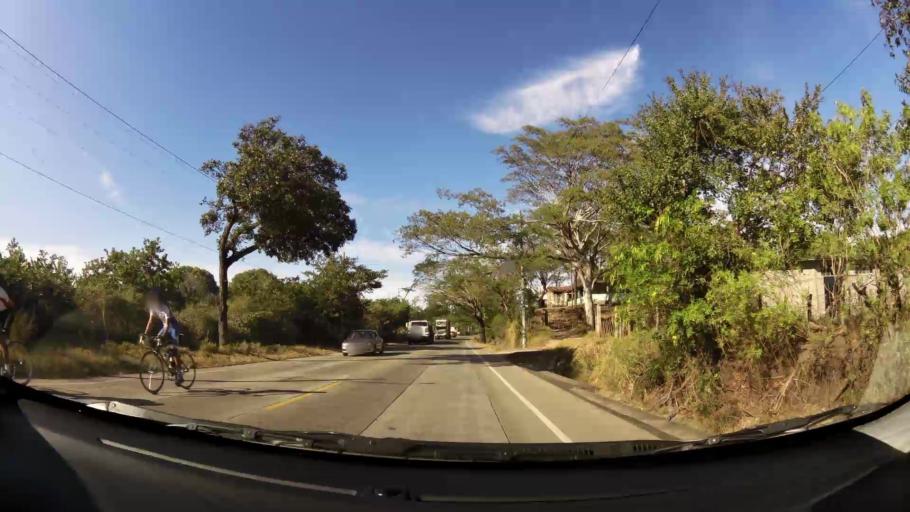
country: SV
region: Santa Ana
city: Texistepeque
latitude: 14.1055
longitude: -89.4997
